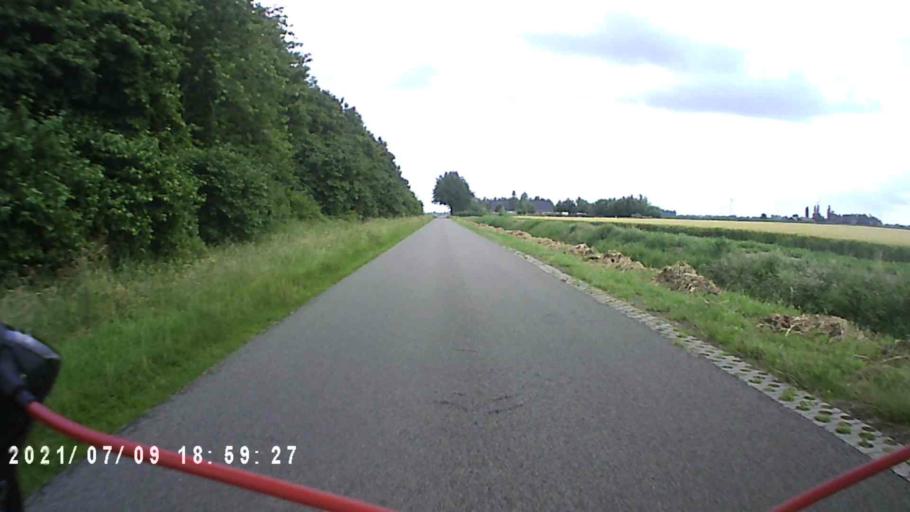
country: NL
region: Groningen
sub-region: Gemeente Veendam
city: Veendam
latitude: 53.0417
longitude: 6.8984
